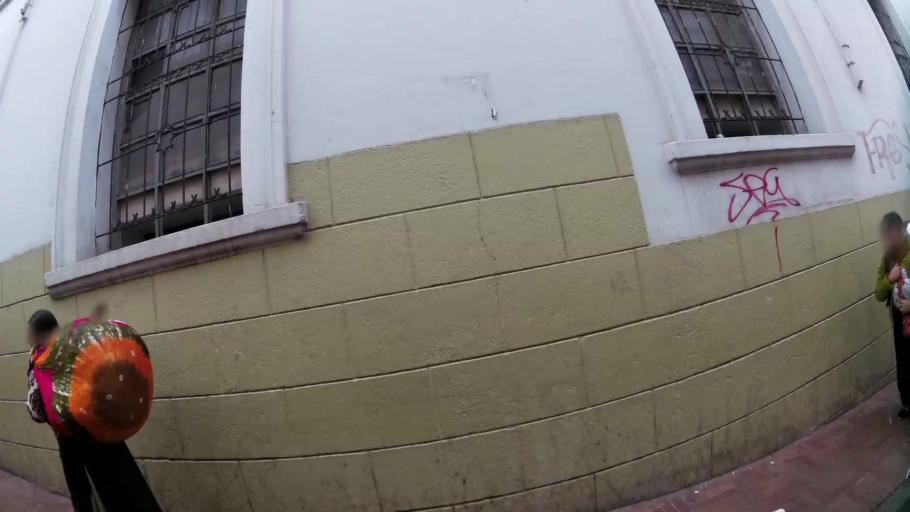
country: EC
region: Pichincha
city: Quito
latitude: -0.2205
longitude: -78.5161
